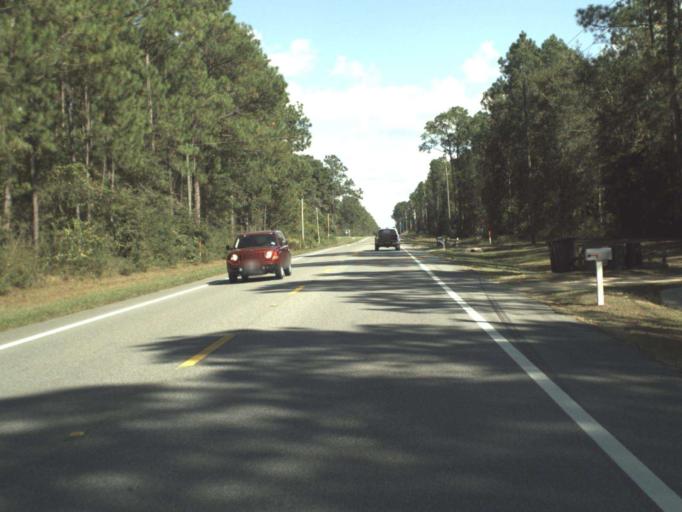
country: US
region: Florida
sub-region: Walton County
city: Freeport
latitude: 30.4768
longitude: -86.0358
